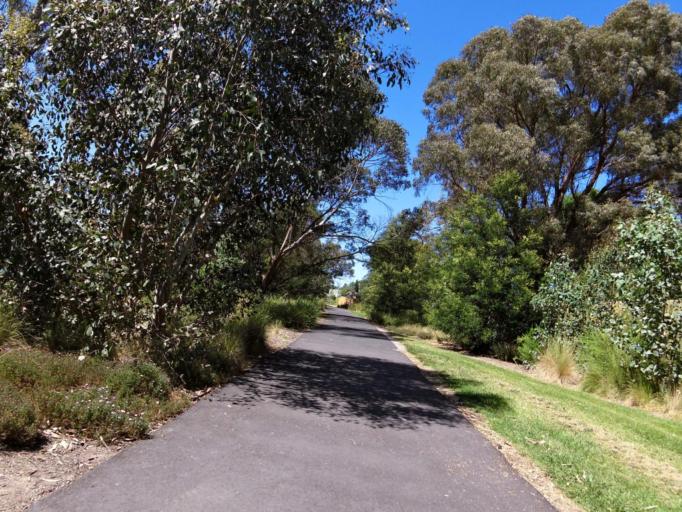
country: AU
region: Victoria
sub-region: Knox
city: Boronia
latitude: -37.8711
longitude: 145.2807
